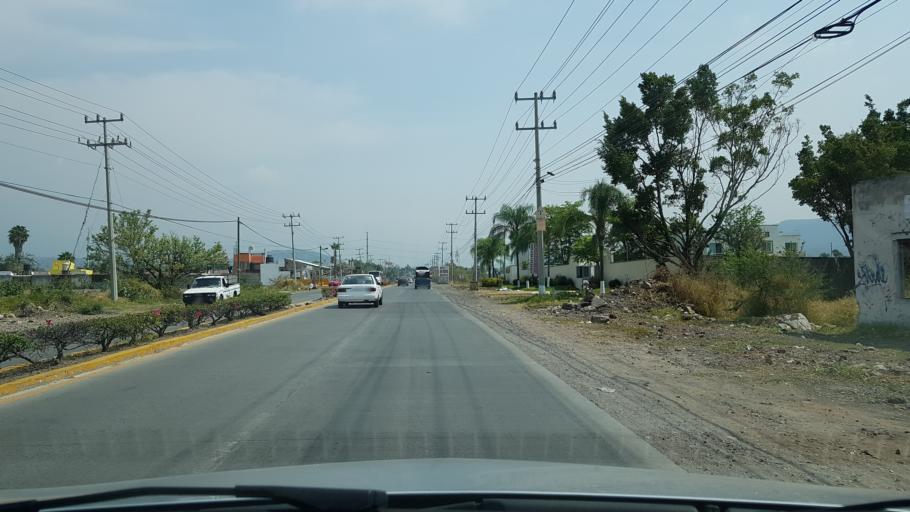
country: MX
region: Morelos
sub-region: Xochitepec
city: Chiconcuac
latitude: 18.8065
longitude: -99.1956
